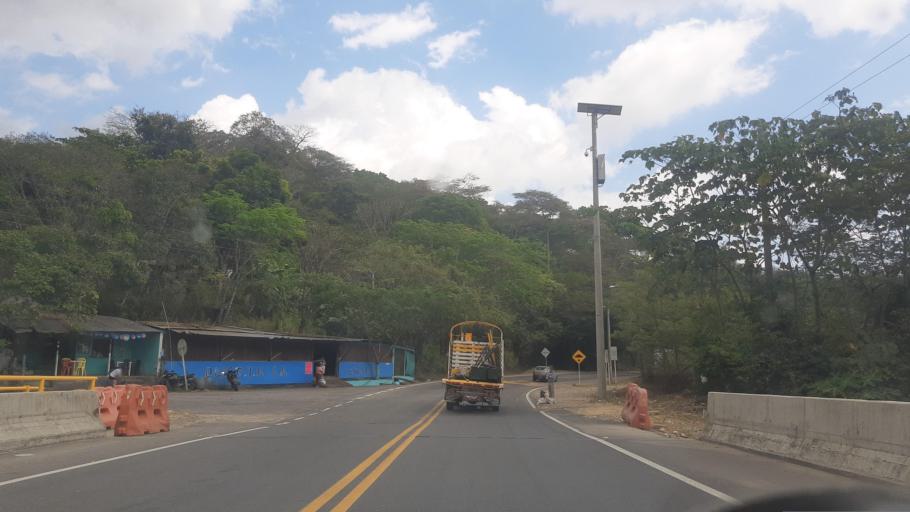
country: CO
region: Casanare
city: Tauramena
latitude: 5.0120
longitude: -72.6857
